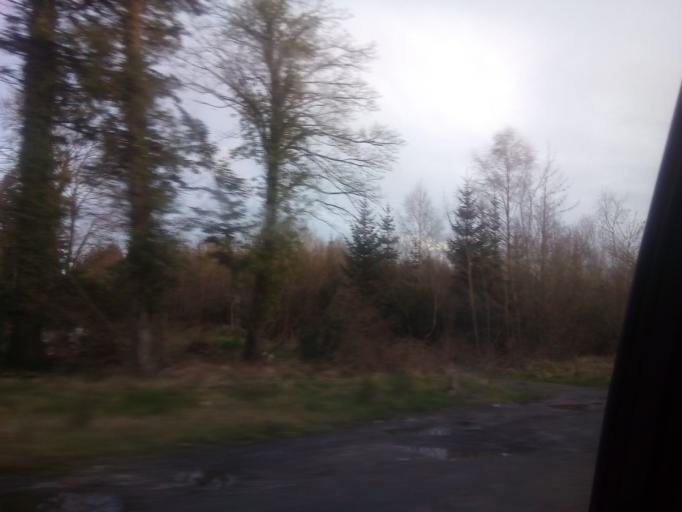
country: IE
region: Leinster
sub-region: Laois
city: Abbeyleix
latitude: 52.8996
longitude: -7.3580
